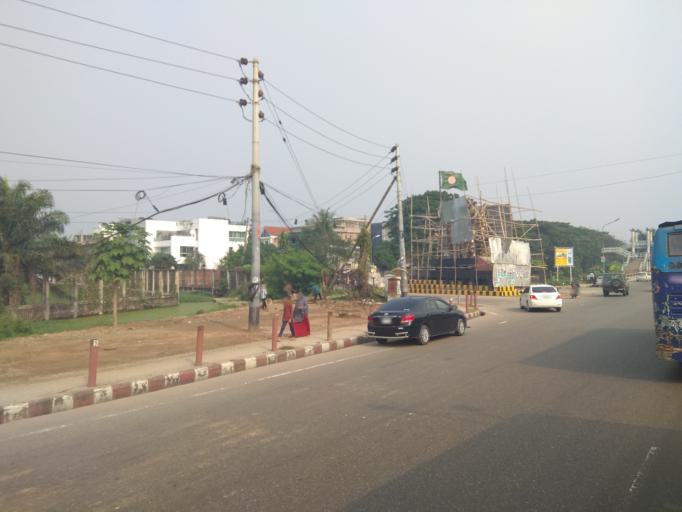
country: BD
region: Dhaka
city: Tungi
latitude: 23.8201
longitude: 90.4168
